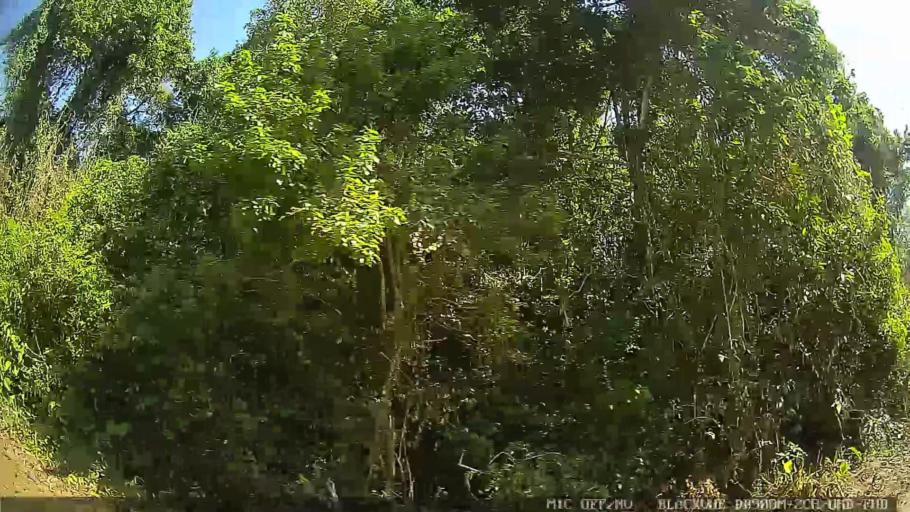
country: BR
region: Sao Paulo
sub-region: Guaruja
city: Guaruja
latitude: -24.0065
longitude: -46.3036
